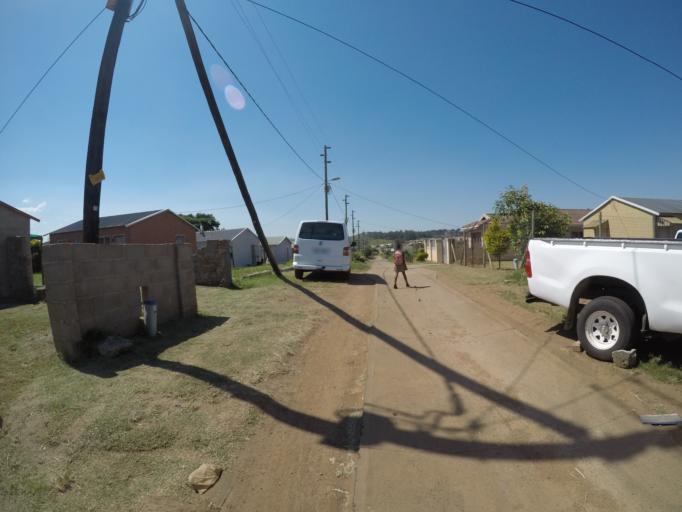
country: ZA
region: KwaZulu-Natal
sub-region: uThungulu District Municipality
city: Empangeni
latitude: -28.7686
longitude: 31.8783
